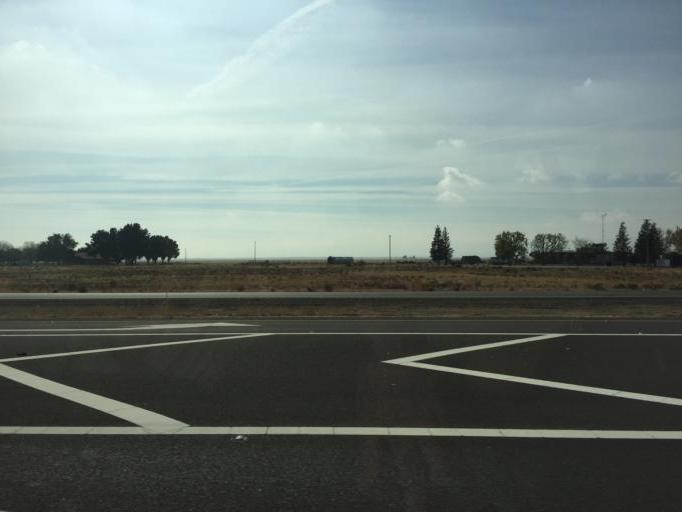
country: US
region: California
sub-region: Kern County
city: Lost Hills
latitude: 35.6152
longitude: -119.8659
